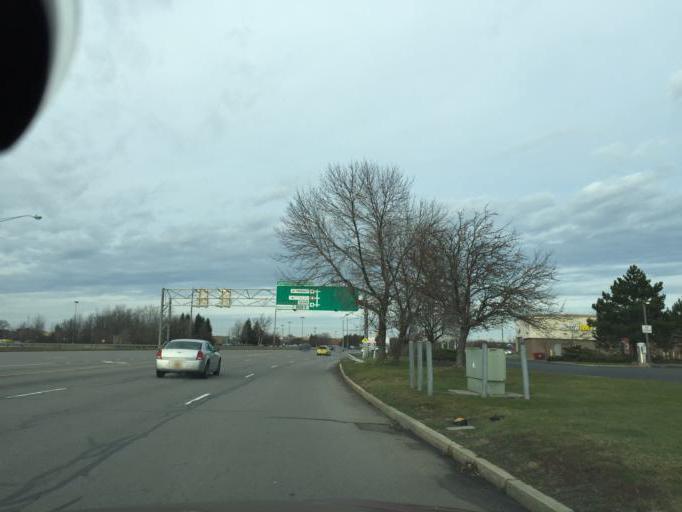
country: US
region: New York
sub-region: Monroe County
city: Rochester
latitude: 43.0784
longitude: -77.6287
